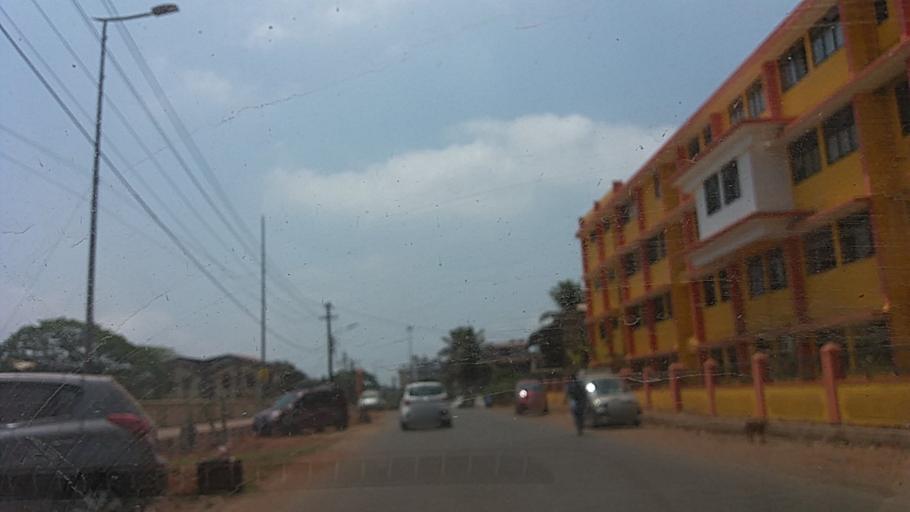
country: IN
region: Goa
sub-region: North Goa
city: Serula
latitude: 15.5267
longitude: 73.8316
